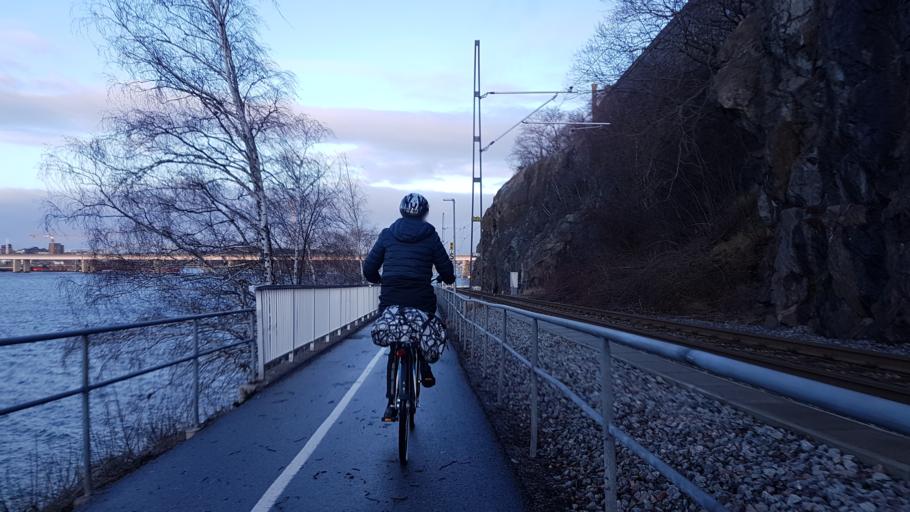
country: SE
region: Stockholm
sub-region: Lidingo
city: Lidingoe
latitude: 59.3582
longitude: 18.1214
